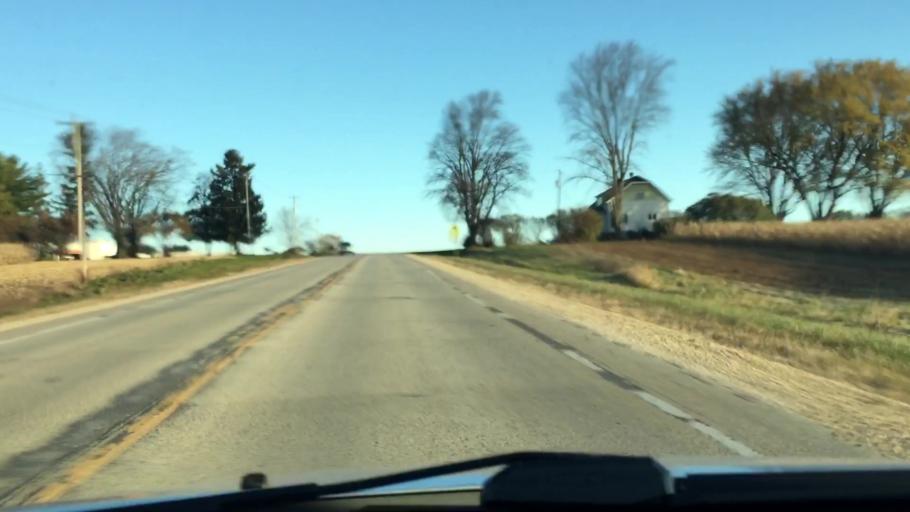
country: US
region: Wisconsin
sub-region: Washington County
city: Hartford
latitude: 43.3152
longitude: -88.4591
